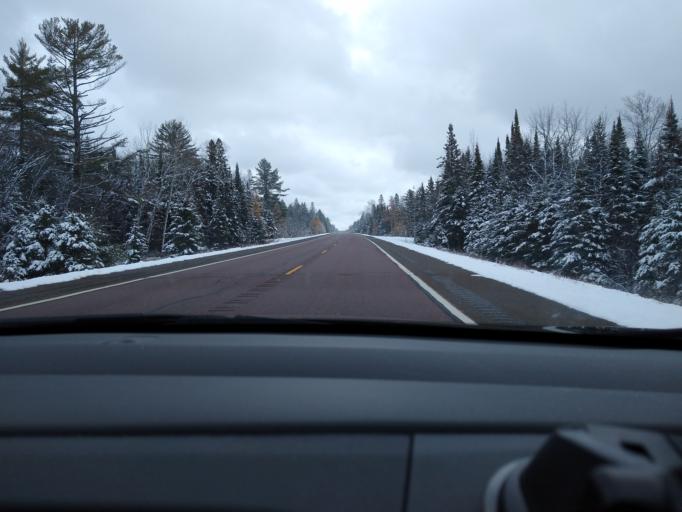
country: US
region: Michigan
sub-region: Iron County
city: Iron River
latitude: 46.1705
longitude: -88.9349
